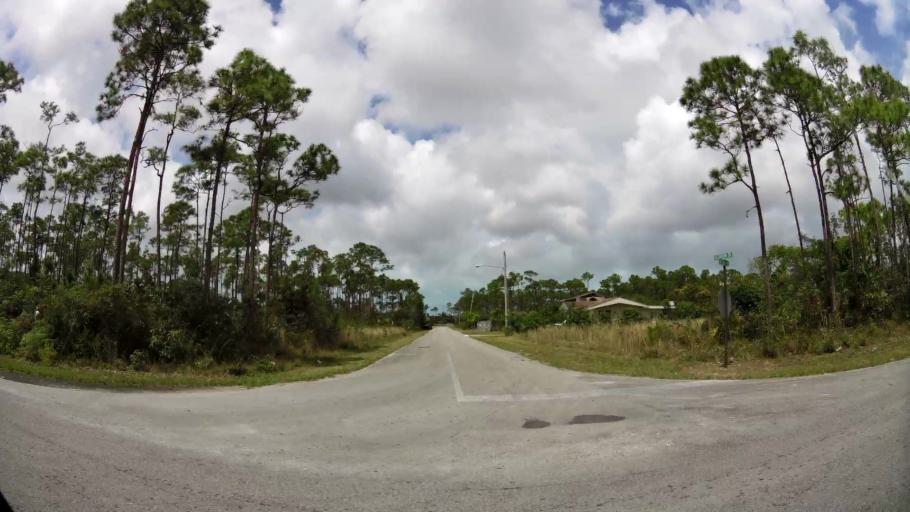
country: BS
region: Freeport
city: Lucaya
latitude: 26.5413
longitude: -78.6474
